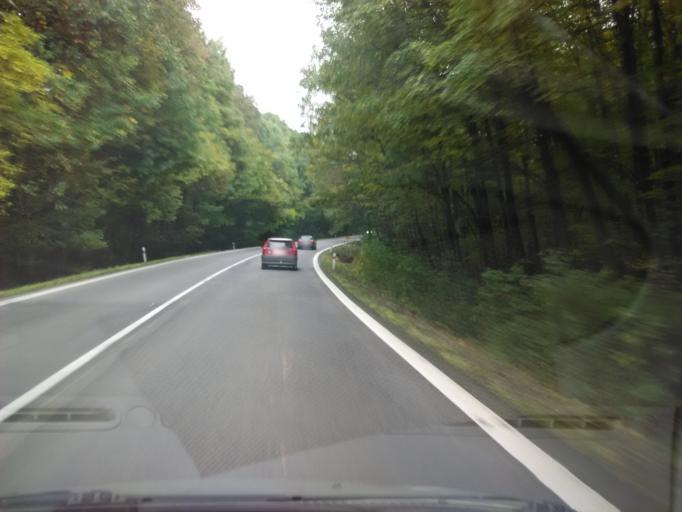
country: SK
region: Nitriansky
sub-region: Okres Nitra
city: Vrable
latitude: 48.2287
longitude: 18.4147
